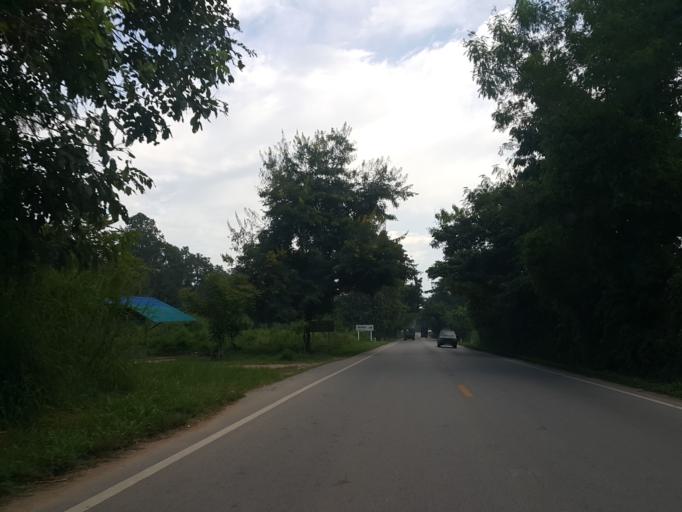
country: TH
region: Chiang Mai
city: Phrao
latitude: 19.2918
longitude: 99.1882
